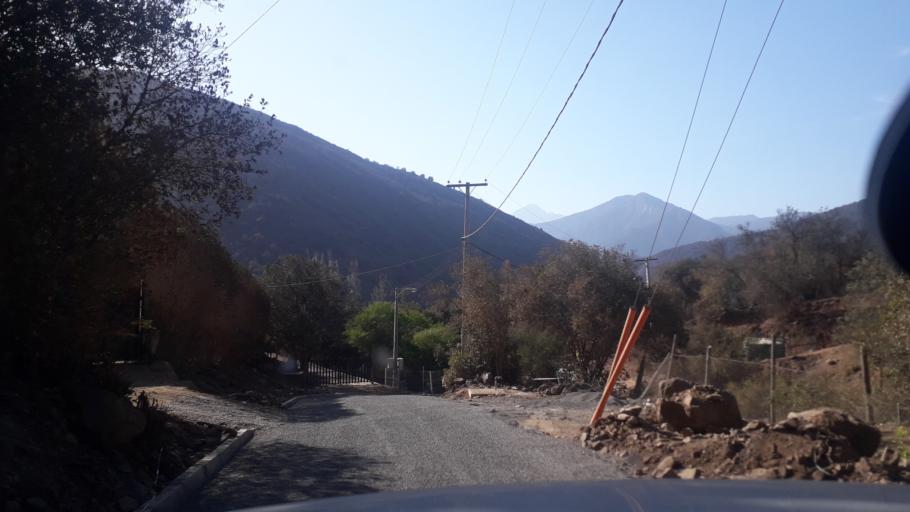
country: CL
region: Valparaiso
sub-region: Provincia de Marga Marga
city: Limache
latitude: -33.0746
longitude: -71.0992
